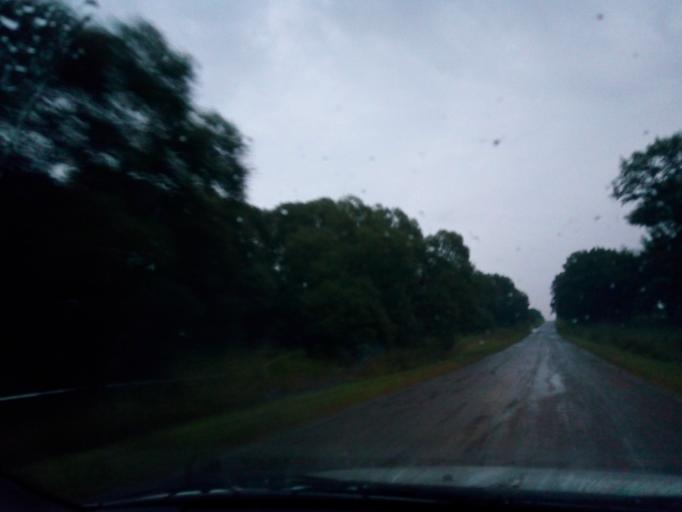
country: RU
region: Primorskiy
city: Lazo
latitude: 45.8701
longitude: 133.7005
